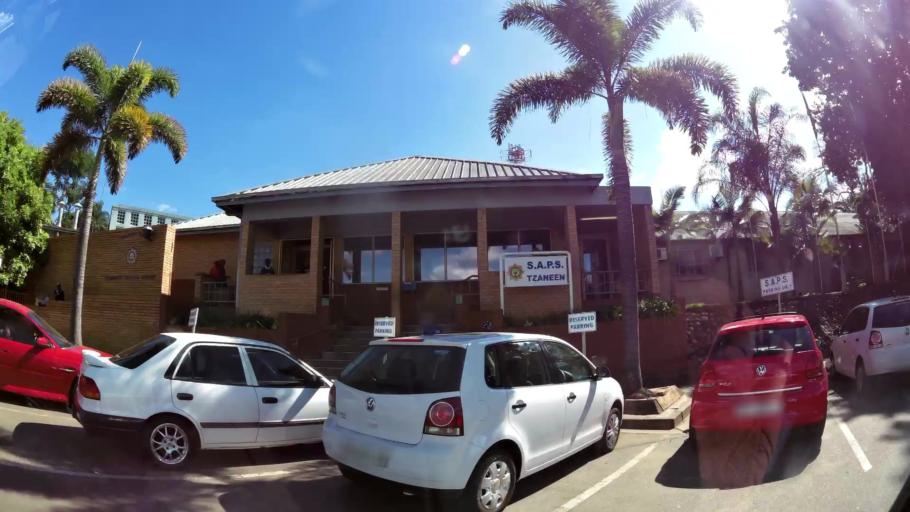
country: ZA
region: Limpopo
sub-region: Mopani District Municipality
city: Tzaneen
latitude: -23.8282
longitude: 30.1622
